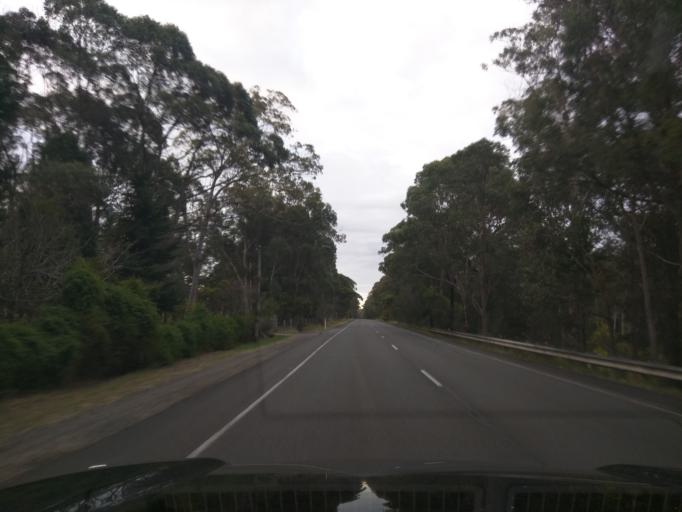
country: AU
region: New South Wales
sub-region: Wollondilly
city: Douglas Park
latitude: -34.2507
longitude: 150.7250
